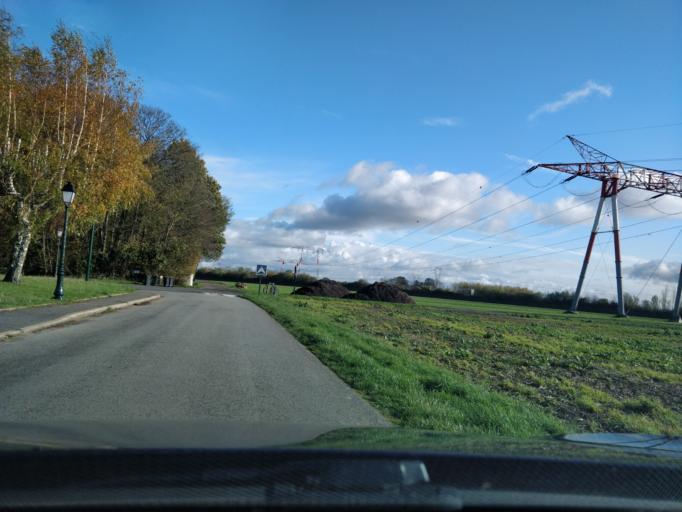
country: FR
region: Ile-de-France
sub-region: Departement de l'Essonne
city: Fontenay-les-Briis
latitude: 48.6434
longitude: 2.1518
